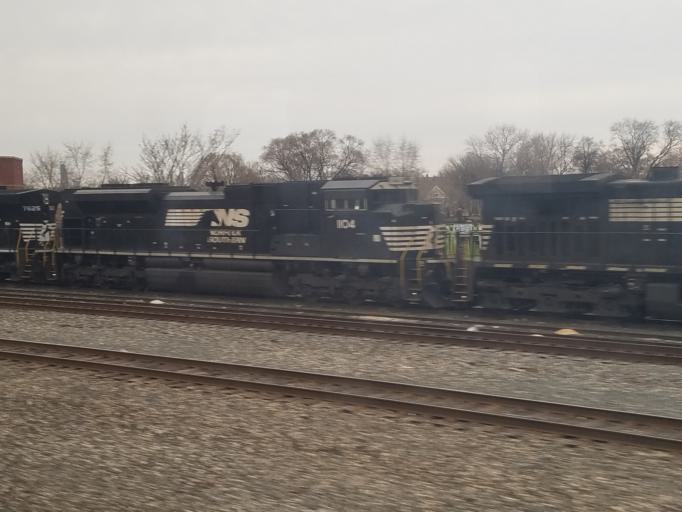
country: US
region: Illinois
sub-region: Cook County
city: Chicago
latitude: 41.7693
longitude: -87.6102
